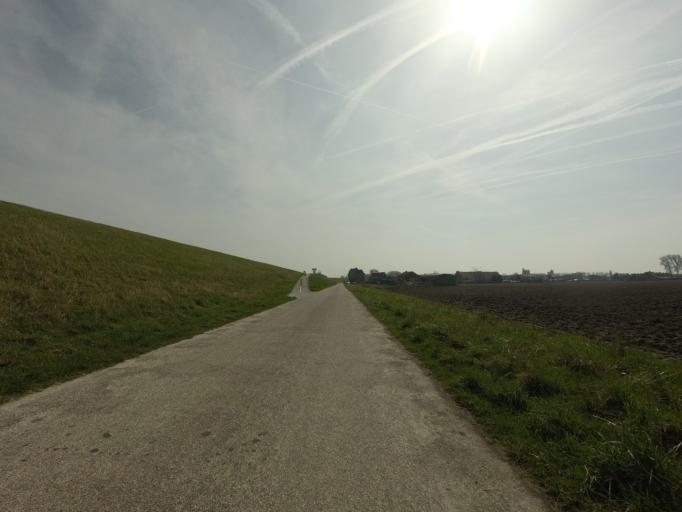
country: NL
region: Zeeland
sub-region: Gemeente Reimerswaal
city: Yerseke
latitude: 51.3867
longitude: 4.0309
